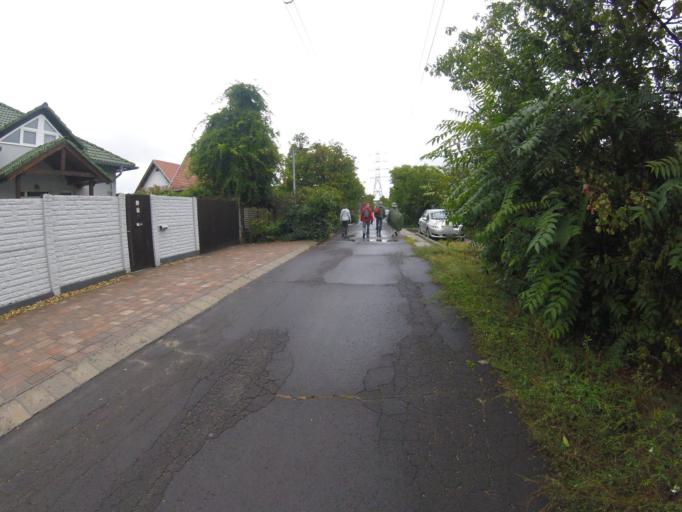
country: HU
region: Pest
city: Dunakeszi
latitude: 47.6554
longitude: 19.1216
